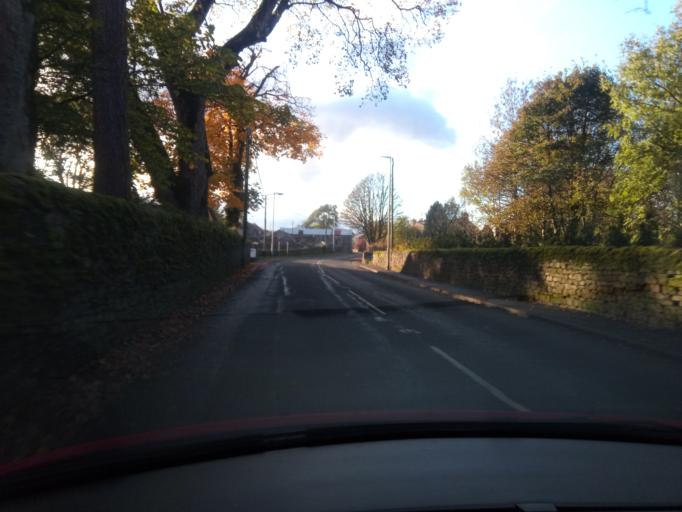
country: GB
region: England
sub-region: County Durham
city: Newbiggin
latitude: 54.7423
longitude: -2.2013
